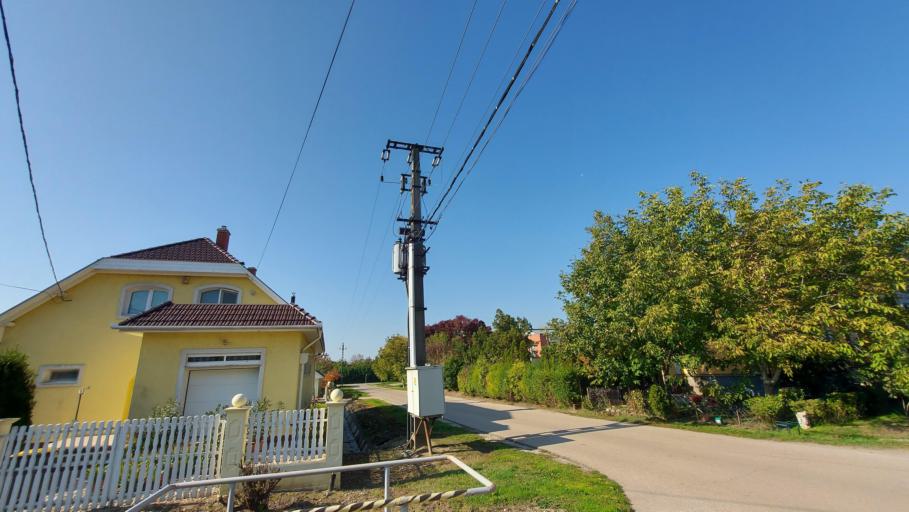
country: HU
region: Fejer
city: Polgardi
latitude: 47.0581
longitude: 18.2975
